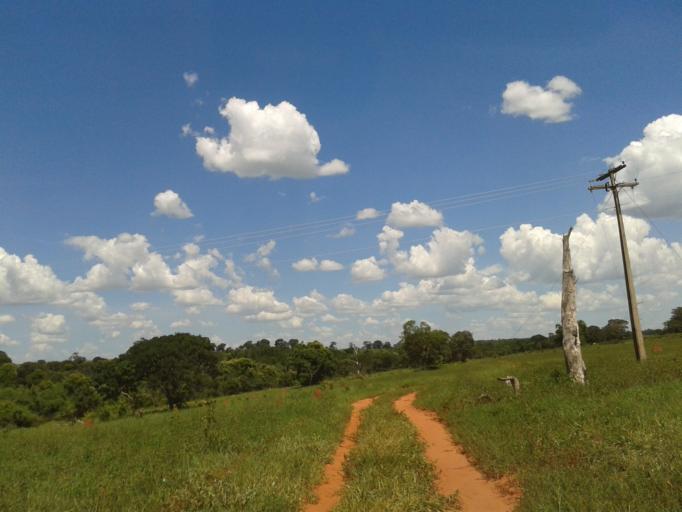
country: BR
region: Minas Gerais
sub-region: Santa Vitoria
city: Santa Vitoria
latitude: -19.1471
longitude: -50.5379
